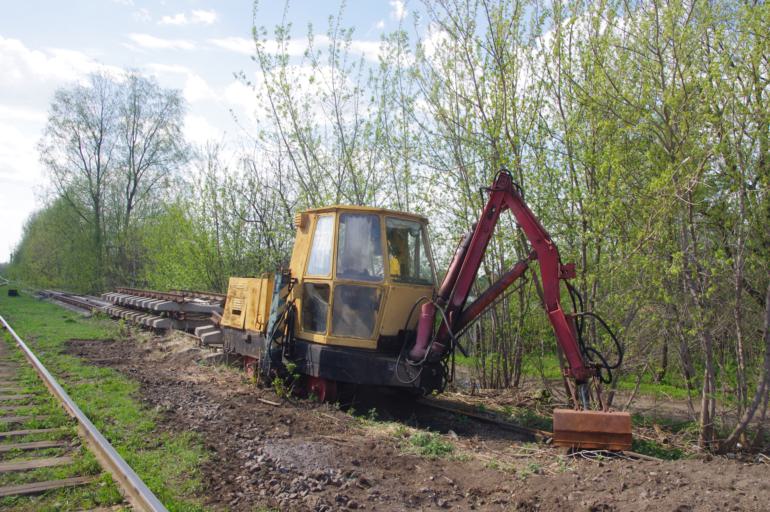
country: RU
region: Moskovskaya
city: Klin
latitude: 56.3318
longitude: 36.7037
